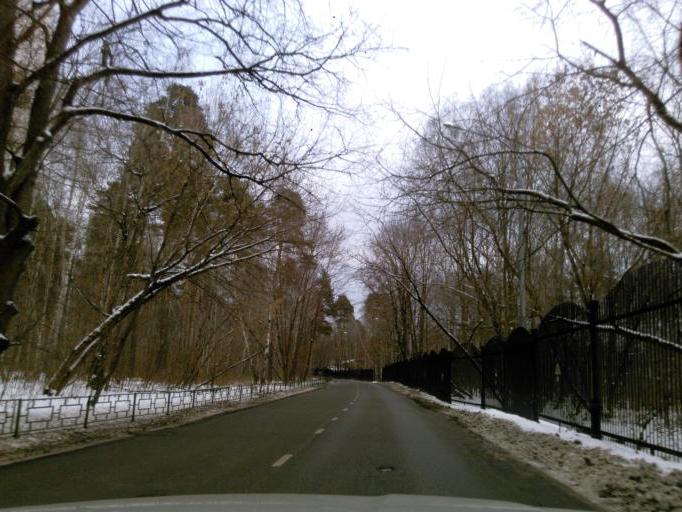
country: RU
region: Moskovskaya
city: Levoberezhnyy
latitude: 55.8268
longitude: 37.4840
